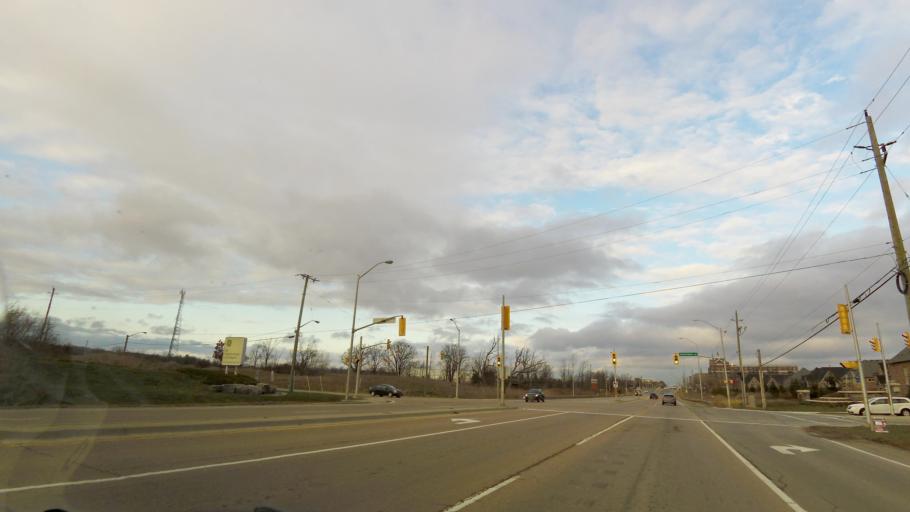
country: CA
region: Ontario
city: Burlington
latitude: 43.4288
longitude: -79.7836
